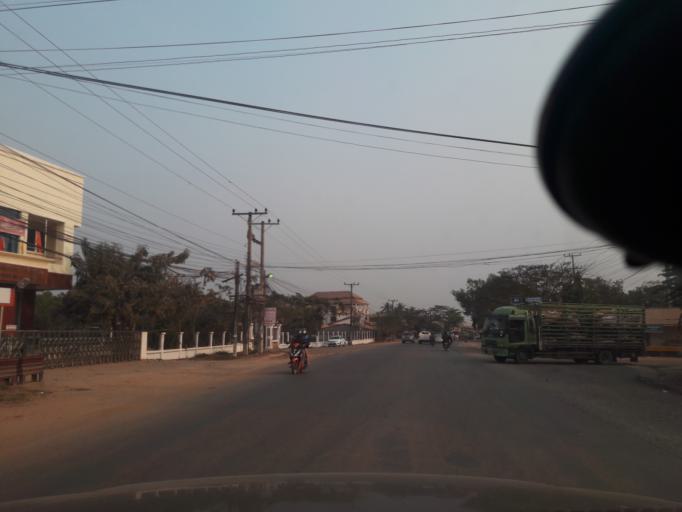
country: LA
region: Vientiane
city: Vientiane
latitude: 18.0655
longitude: 102.5371
